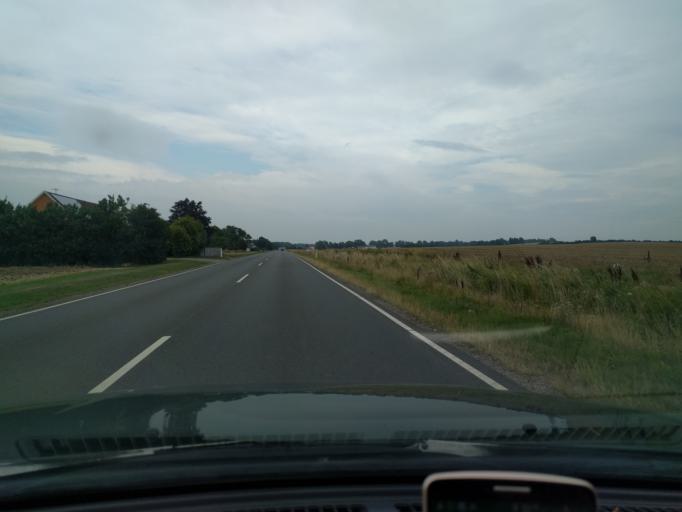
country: DK
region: Zealand
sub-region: Slagelse Kommune
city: Korsor
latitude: 55.3210
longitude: 11.2037
